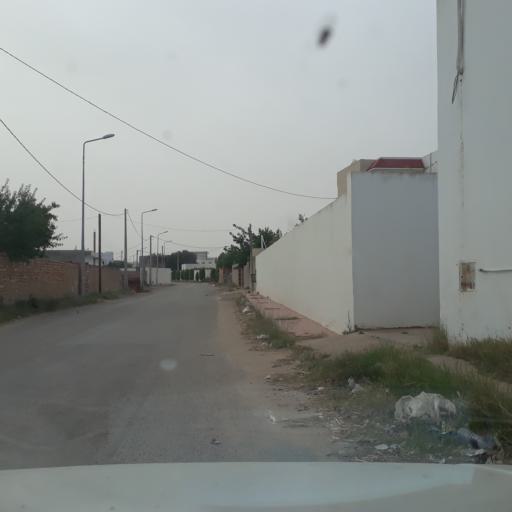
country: TN
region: Safaqis
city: Al Qarmadah
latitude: 34.8193
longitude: 10.7770
